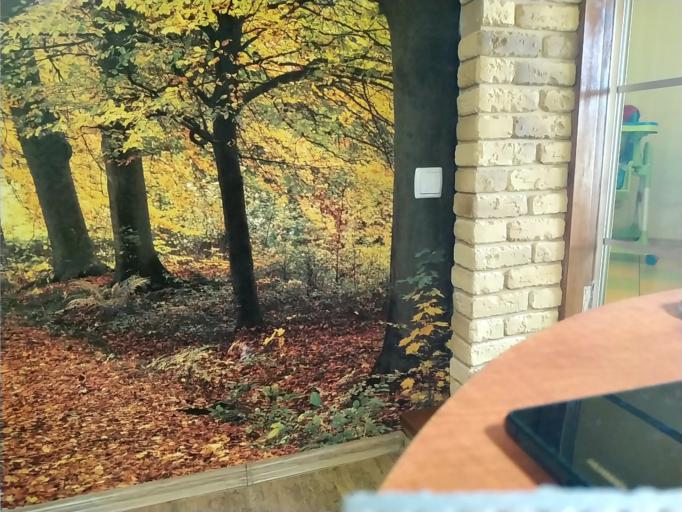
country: RU
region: Kaluga
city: Kondrovo
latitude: 54.8063
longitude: 35.9519
